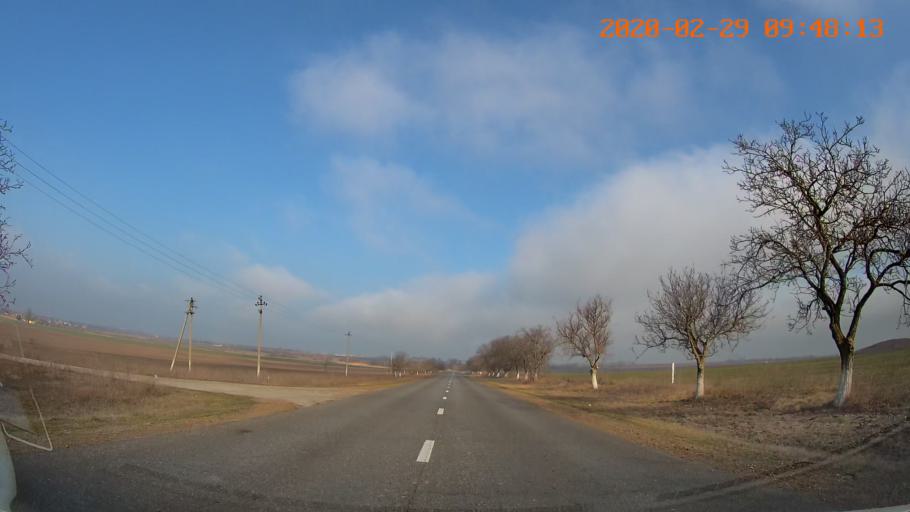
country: MD
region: Telenesti
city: Crasnoe
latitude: 46.6855
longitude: 29.7859
